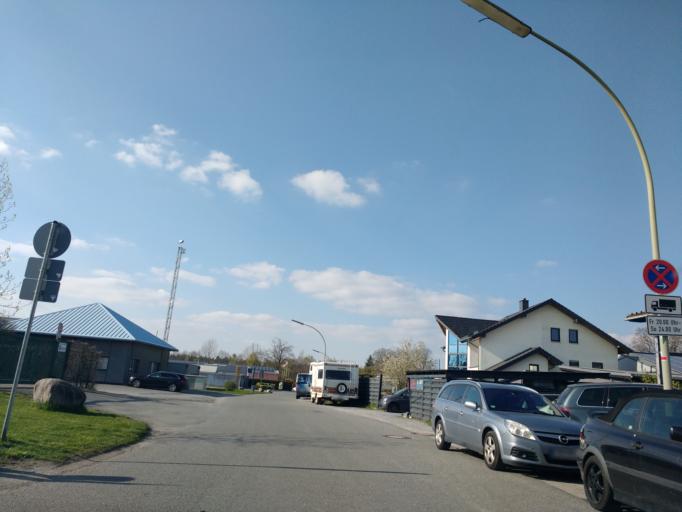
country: DE
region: North Rhine-Westphalia
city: Bad Lippspringe
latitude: 51.8030
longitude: 8.8218
